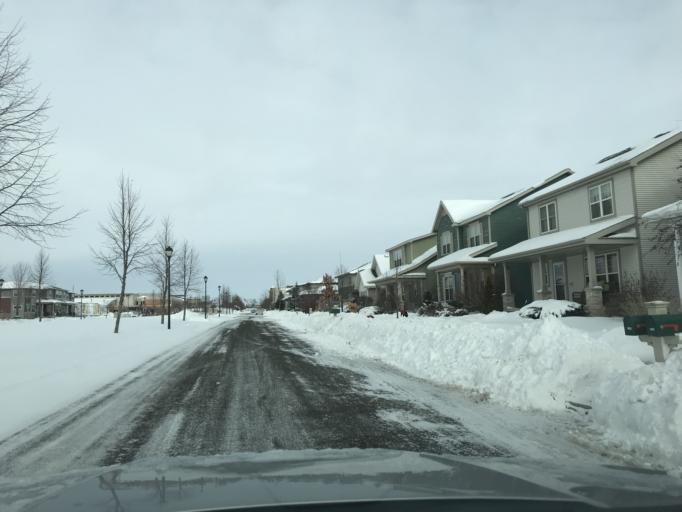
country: US
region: Wisconsin
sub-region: Dane County
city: Sun Prairie
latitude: 43.1587
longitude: -89.2618
